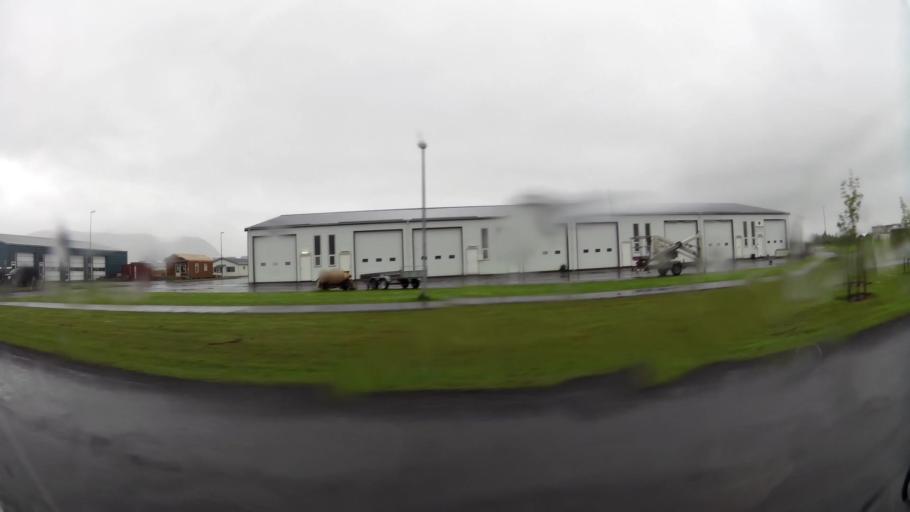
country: IS
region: South
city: Selfoss
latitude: 63.9266
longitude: -21.0162
